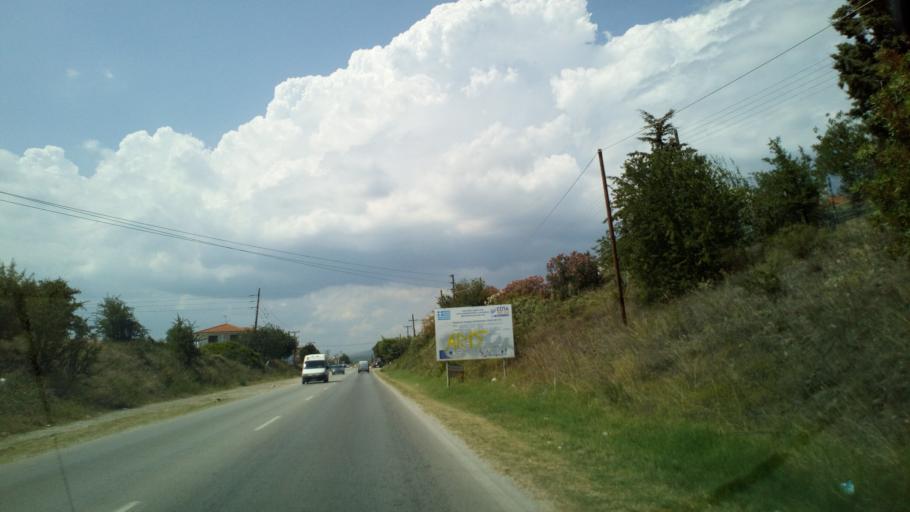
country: GR
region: Central Macedonia
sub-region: Nomos Chalkidikis
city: Nikiti
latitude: 40.2170
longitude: 23.6775
